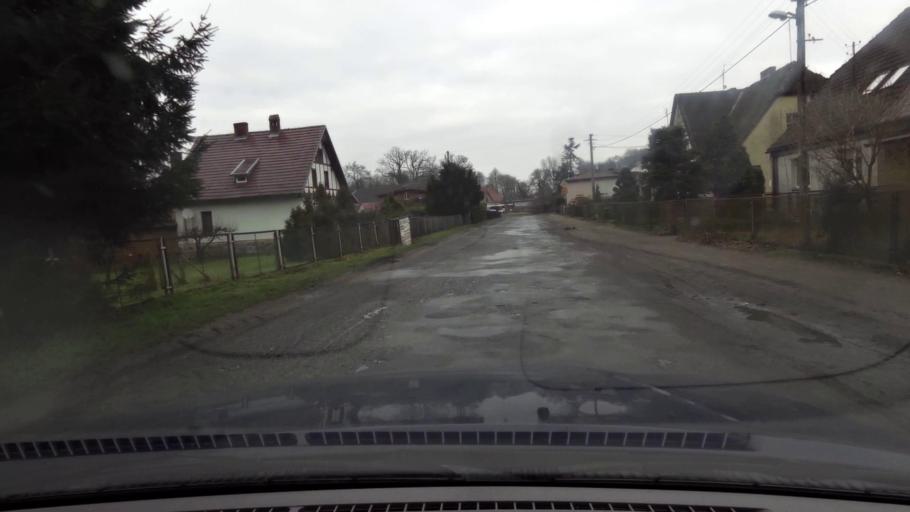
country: PL
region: West Pomeranian Voivodeship
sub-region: Powiat stargardzki
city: Marianowo
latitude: 53.3367
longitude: 15.1937
